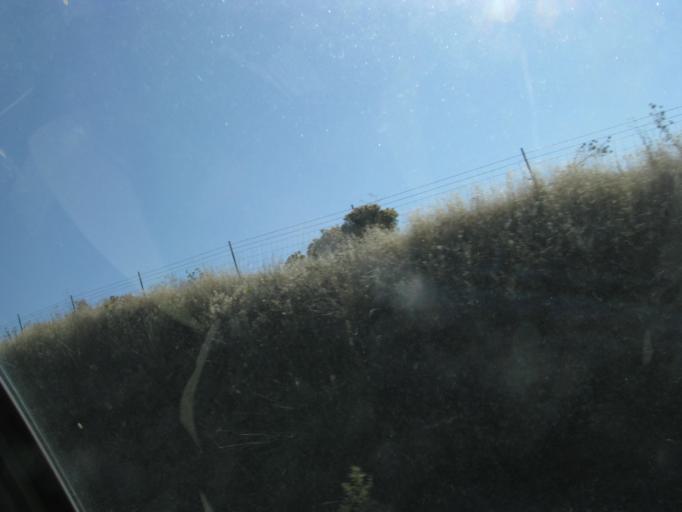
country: US
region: Washington
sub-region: Asotin County
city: Asotin
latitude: 46.3285
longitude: -117.0638
